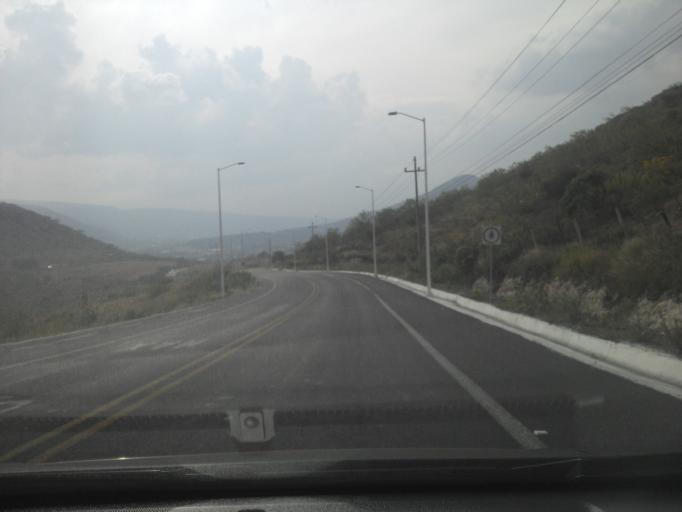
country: MX
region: Jalisco
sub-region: Tlajomulco de Zuniga
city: Lomas del Sur
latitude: 20.4851
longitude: -103.4281
